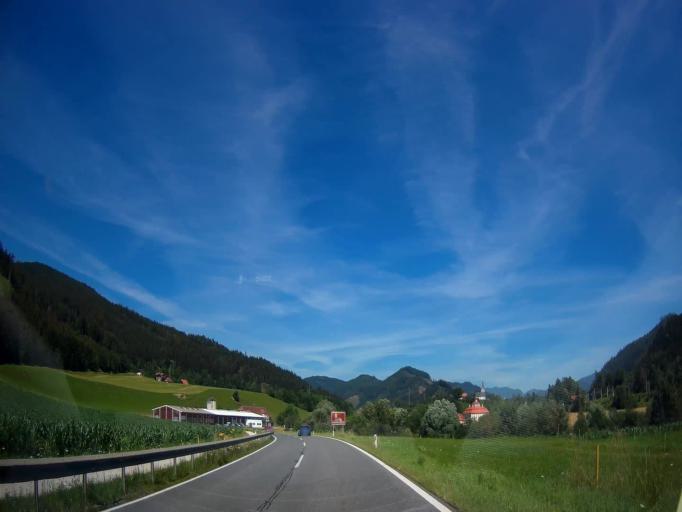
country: AT
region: Carinthia
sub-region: Politischer Bezirk Sankt Veit an der Glan
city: Althofen
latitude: 46.8853
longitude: 14.4435
